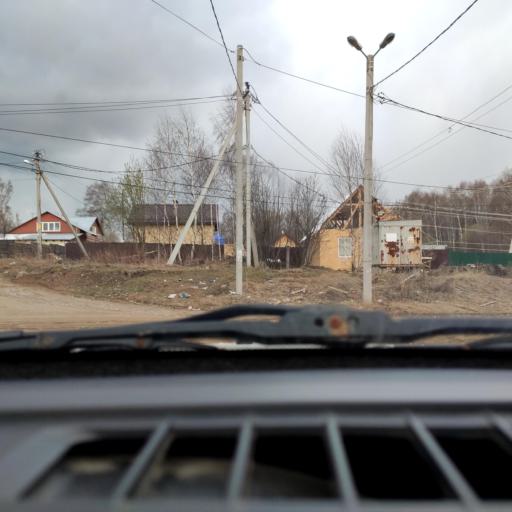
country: RU
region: Perm
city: Perm
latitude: 58.0839
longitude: 56.3643
